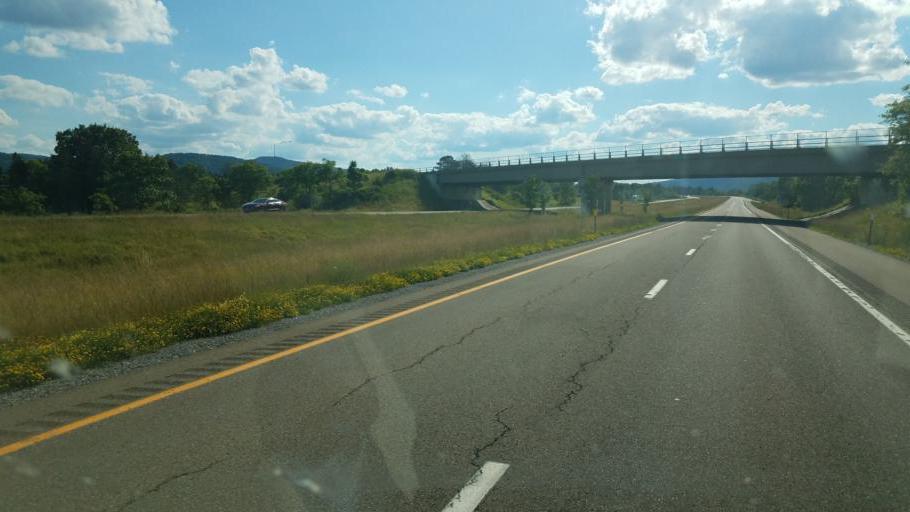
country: US
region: New York
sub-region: Cattaraugus County
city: Allegany
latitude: 42.1029
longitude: -78.5062
